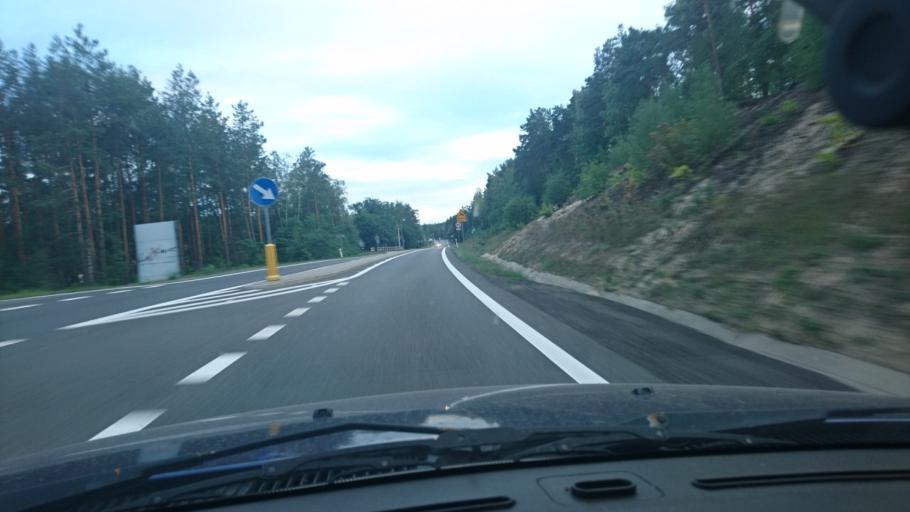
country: PL
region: Silesian Voivodeship
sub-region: Powiat tarnogorski
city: Tworog
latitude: 50.5973
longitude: 18.7027
